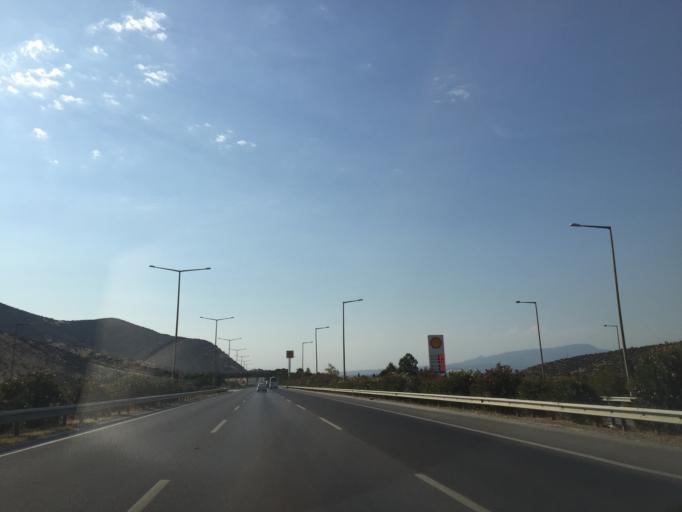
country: TR
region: Izmir
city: Belevi
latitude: 38.0669
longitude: 27.4146
